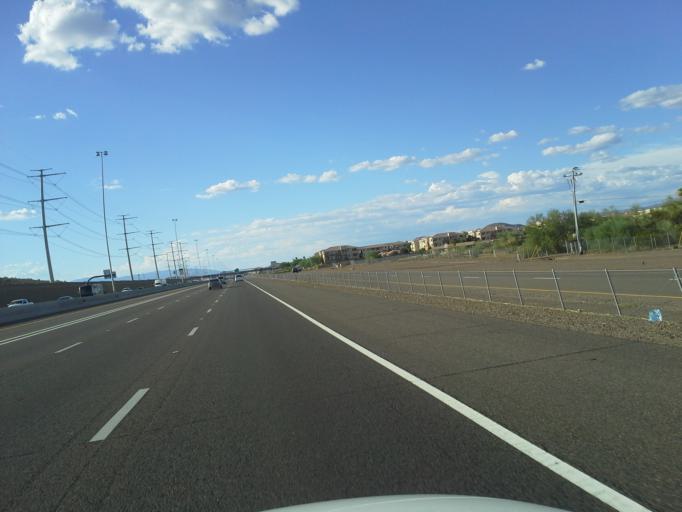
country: US
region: Arizona
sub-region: Maricopa County
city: Anthem
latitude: 33.7375
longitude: -112.1225
